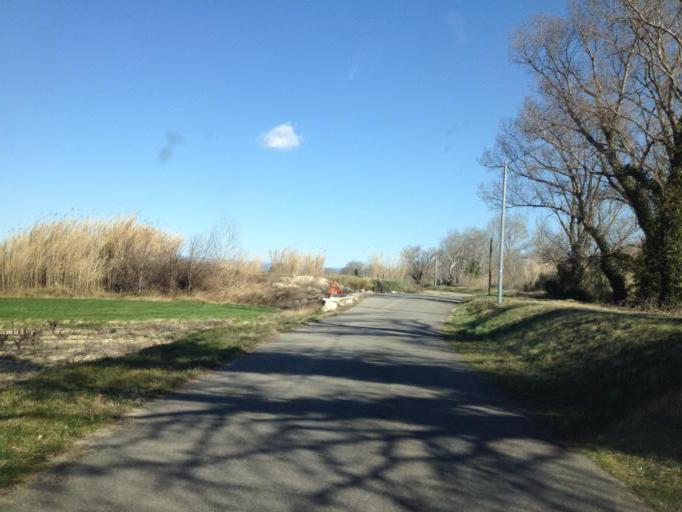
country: FR
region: Provence-Alpes-Cote d'Azur
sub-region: Departement du Vaucluse
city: Bedarrides
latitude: 44.0397
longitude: 4.9104
